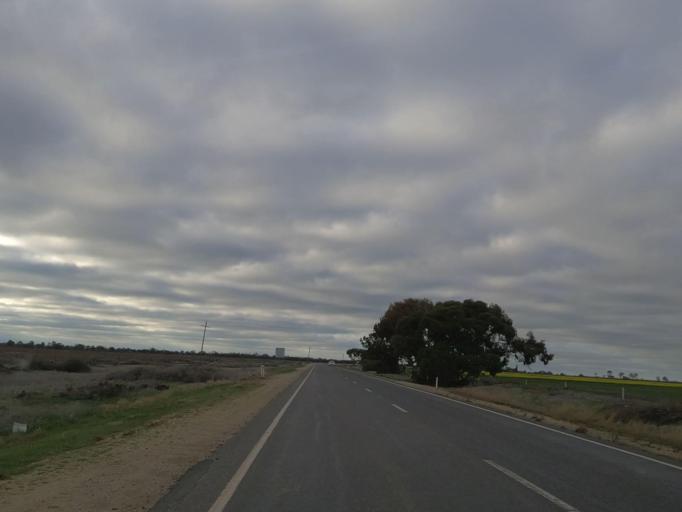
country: AU
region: Victoria
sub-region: Swan Hill
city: Swan Hill
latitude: -35.8308
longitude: 143.9442
